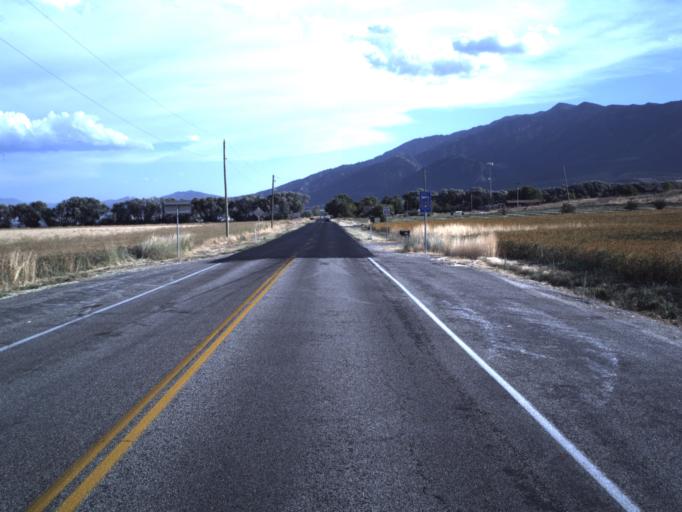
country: US
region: Utah
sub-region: Cache County
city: Mendon
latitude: 41.7499
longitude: -111.9794
